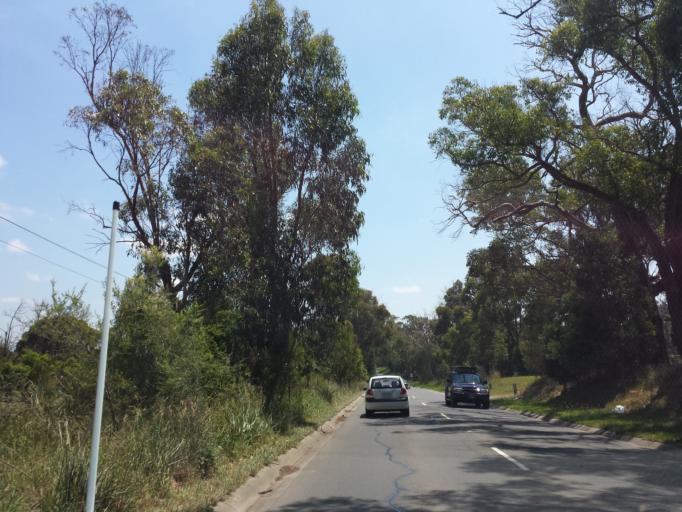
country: AU
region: Victoria
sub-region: Maroondah
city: Kilsyth South
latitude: -37.8335
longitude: 145.3187
